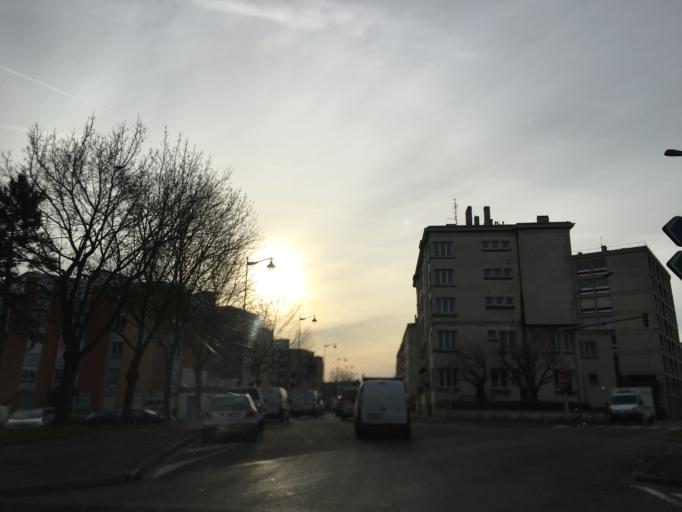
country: FR
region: Nord-Pas-de-Calais
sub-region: Departement du Pas-de-Calais
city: Arras
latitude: 50.2927
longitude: 2.7825
